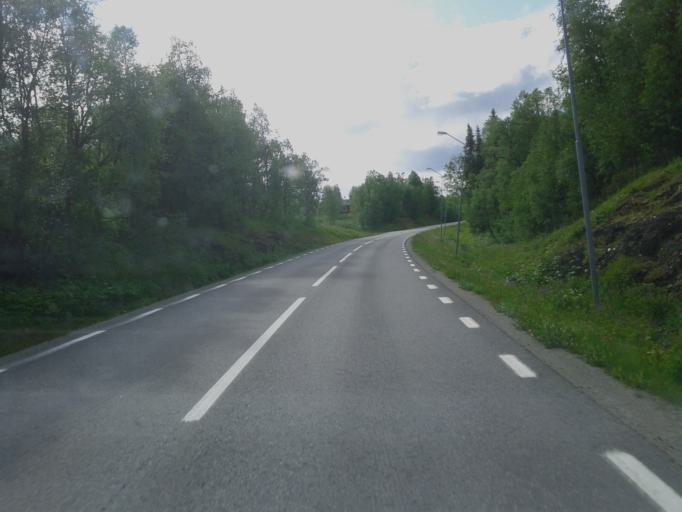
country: NO
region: Nordland
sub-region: Rana
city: Mo i Rana
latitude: 65.7102
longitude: 15.2382
